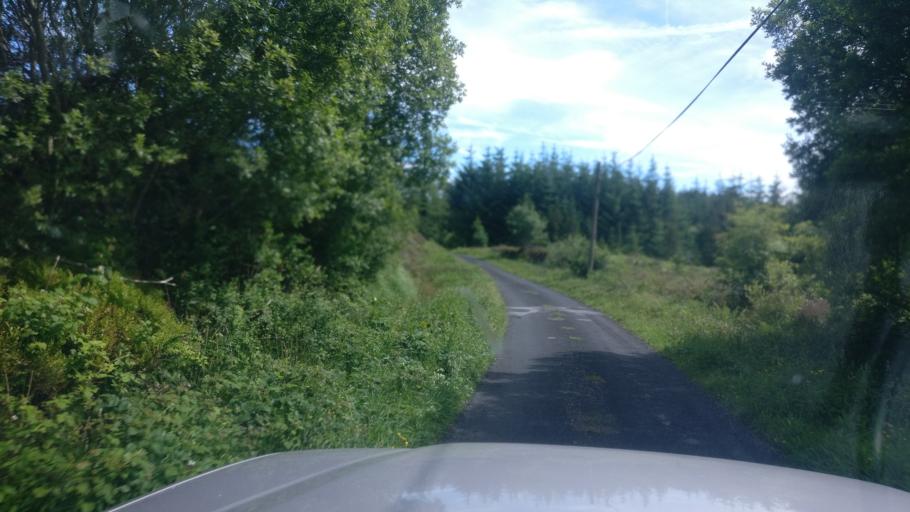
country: IE
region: Connaught
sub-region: County Galway
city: Gort
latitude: 53.0650
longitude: -8.6989
